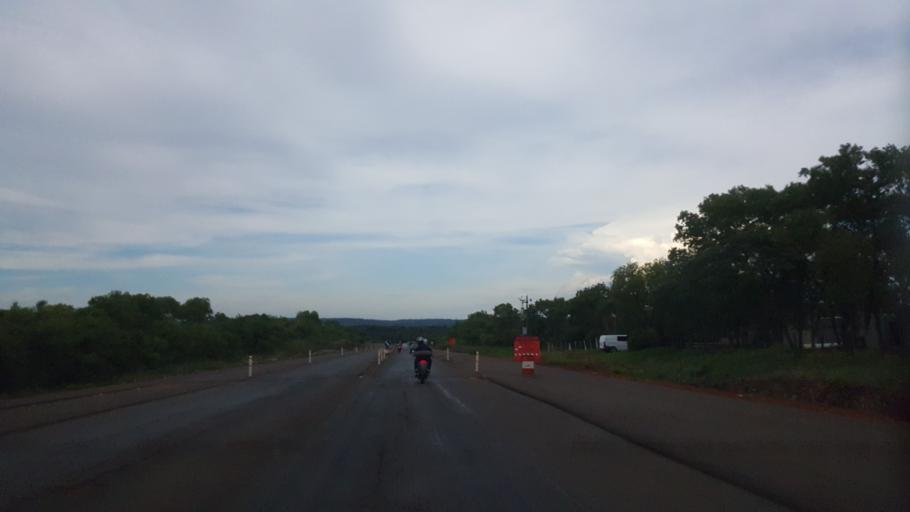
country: AR
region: Misiones
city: Santa Ana
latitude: -27.4104
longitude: -55.6083
